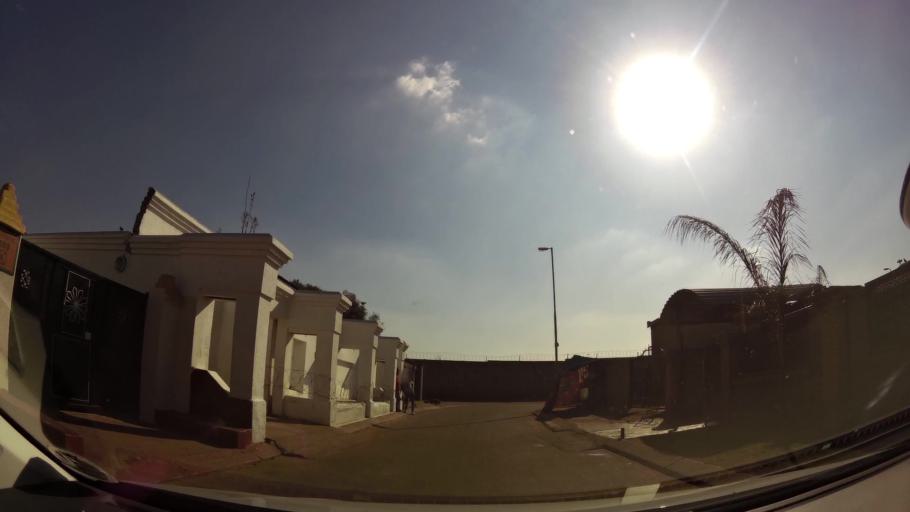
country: ZA
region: Gauteng
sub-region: City of Johannesburg Metropolitan Municipality
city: Soweto
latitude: -26.2806
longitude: 27.8648
